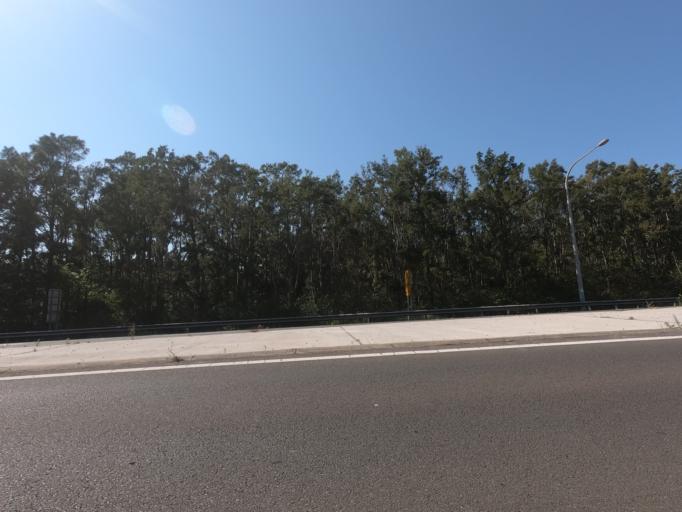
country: AU
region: New South Wales
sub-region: Wollongong
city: Mount Saint Thomas
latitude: -34.4547
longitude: 150.8558
